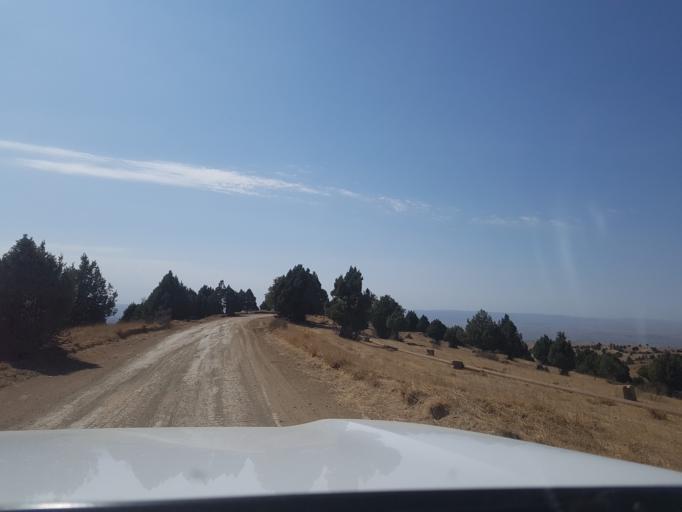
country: TM
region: Ahal
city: Baharly
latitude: 38.3177
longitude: 56.9542
